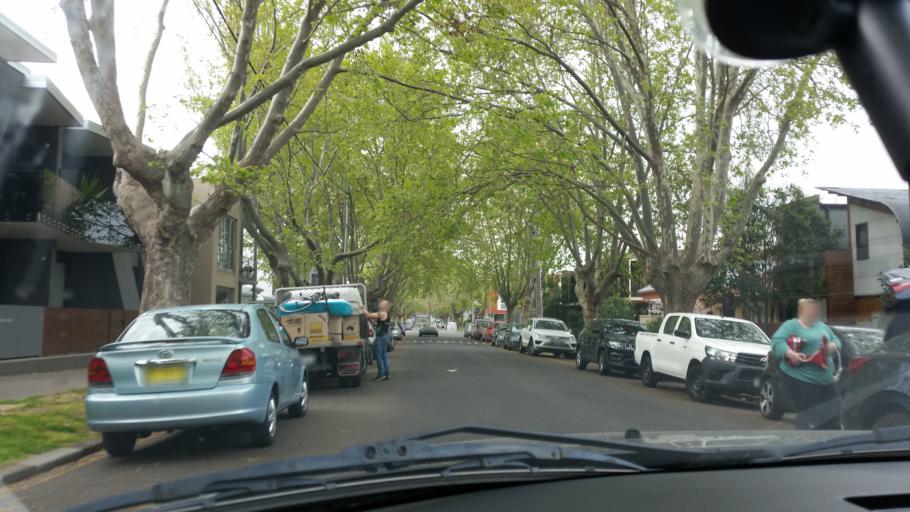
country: AU
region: Victoria
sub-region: Moonee Valley
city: Flemington
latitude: -37.7923
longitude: 144.9314
